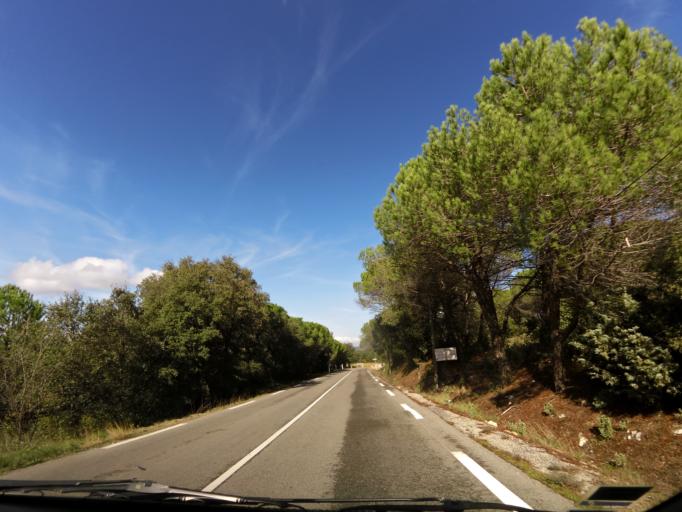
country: FR
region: Languedoc-Roussillon
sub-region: Departement du Gard
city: Villevieille
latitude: 43.8765
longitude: 4.0951
